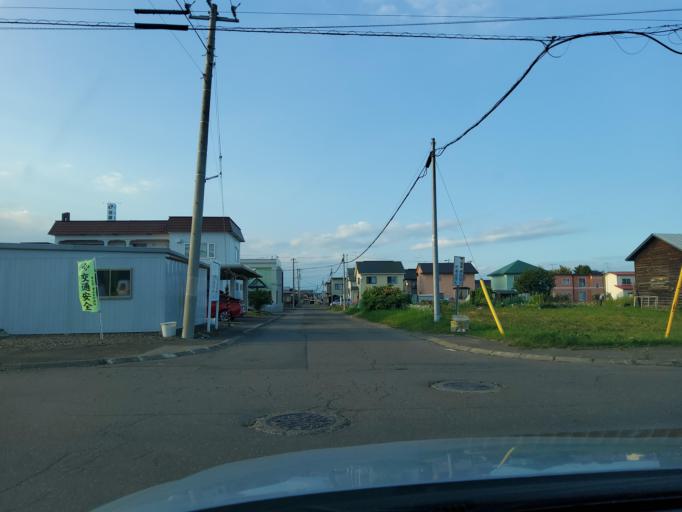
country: JP
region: Hokkaido
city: Obihiro
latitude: 42.9313
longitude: 143.1881
